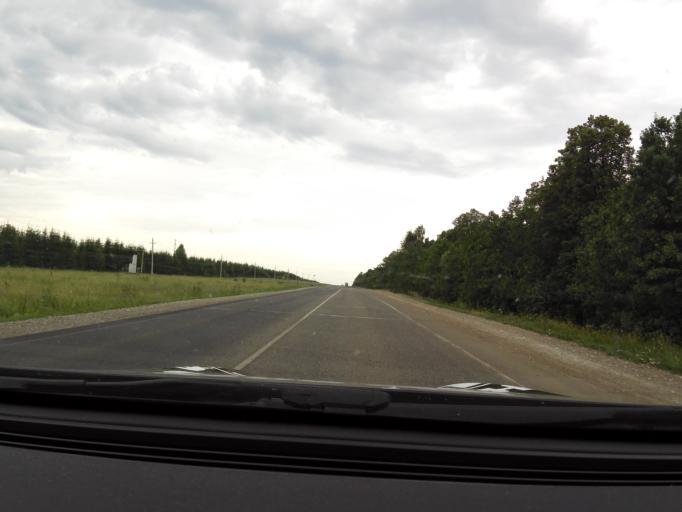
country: RU
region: Bashkortostan
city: Kudeyevskiy
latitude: 54.8074
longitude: 56.6330
